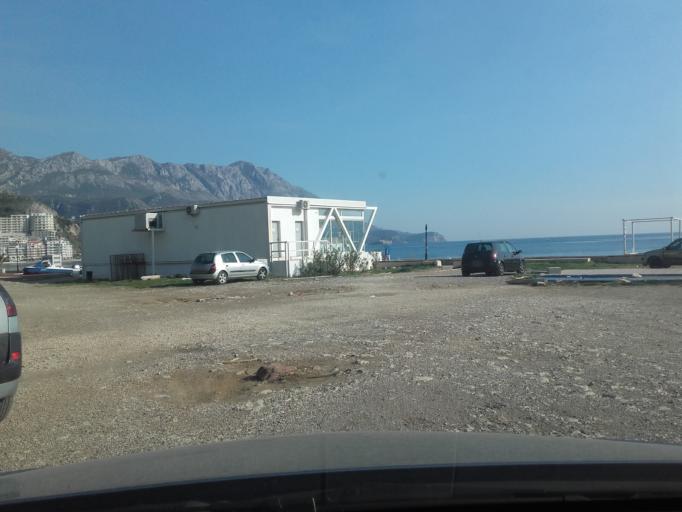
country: ME
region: Budva
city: Budva
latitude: 42.2819
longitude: 18.8729
